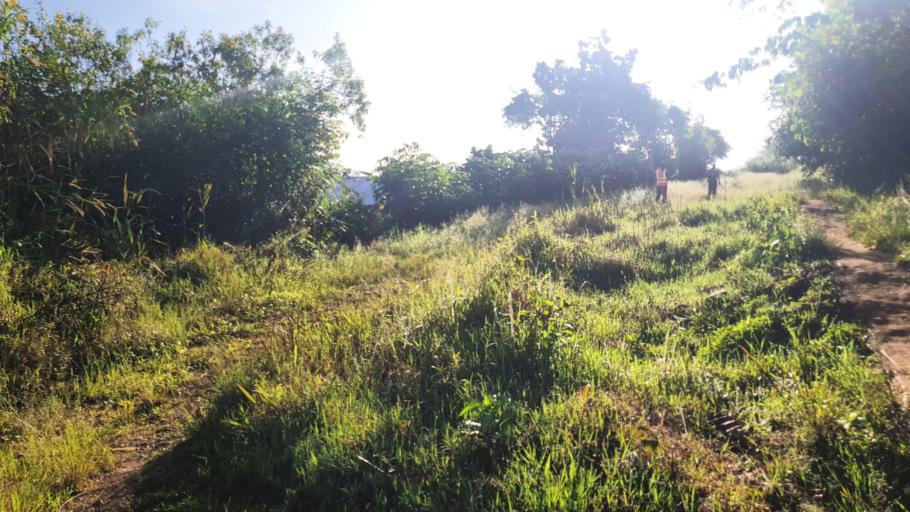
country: PG
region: Western Highlands
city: Rauna
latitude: -5.8002
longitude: 144.3628
